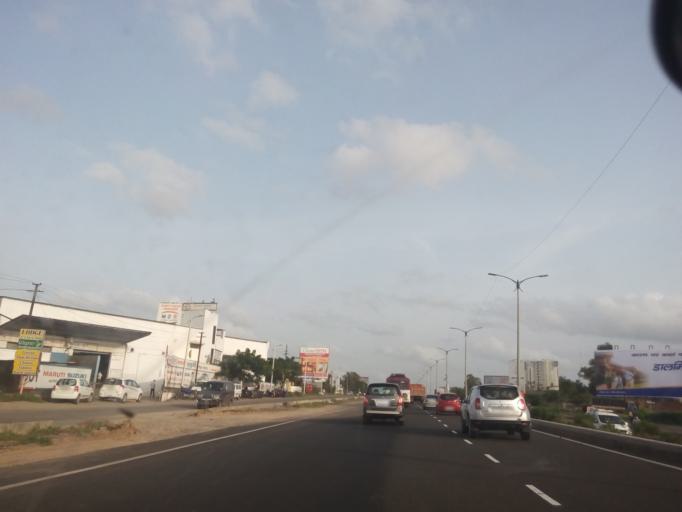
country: IN
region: Maharashtra
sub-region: Pune Division
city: Pimpri
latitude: 18.6267
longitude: 73.7439
